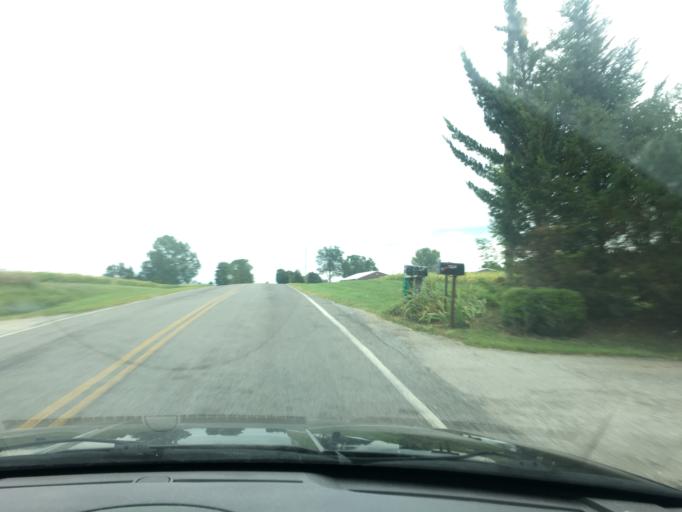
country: US
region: Ohio
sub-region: Logan County
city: West Liberty
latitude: 40.1930
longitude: -83.7690
